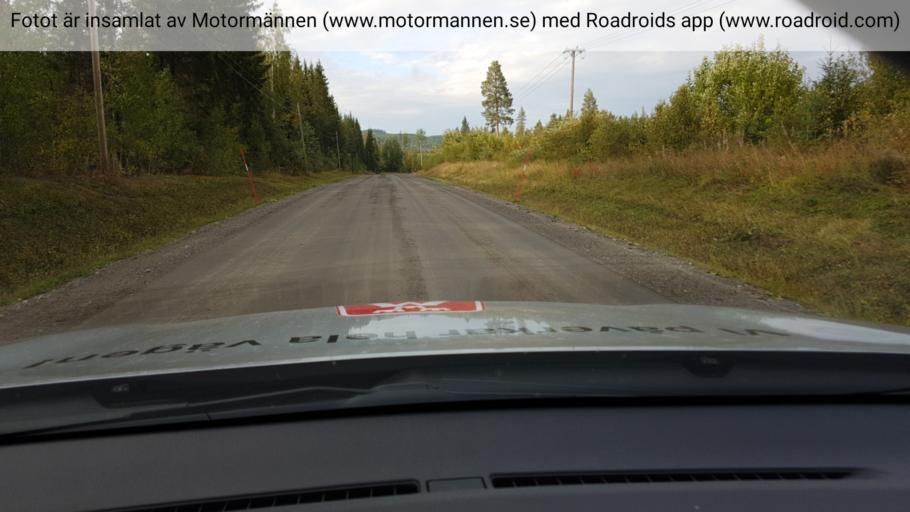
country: SE
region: Jaemtland
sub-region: Stroemsunds Kommun
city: Stroemsund
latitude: 63.9823
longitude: 15.8189
